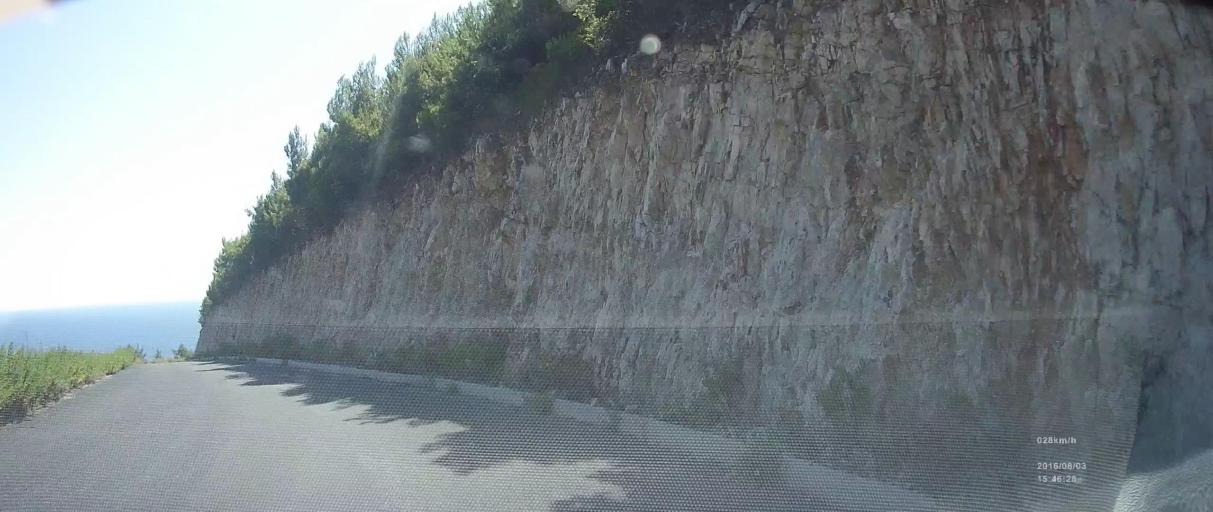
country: HR
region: Dubrovacko-Neretvanska
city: Blato
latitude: 42.7366
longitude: 17.5144
